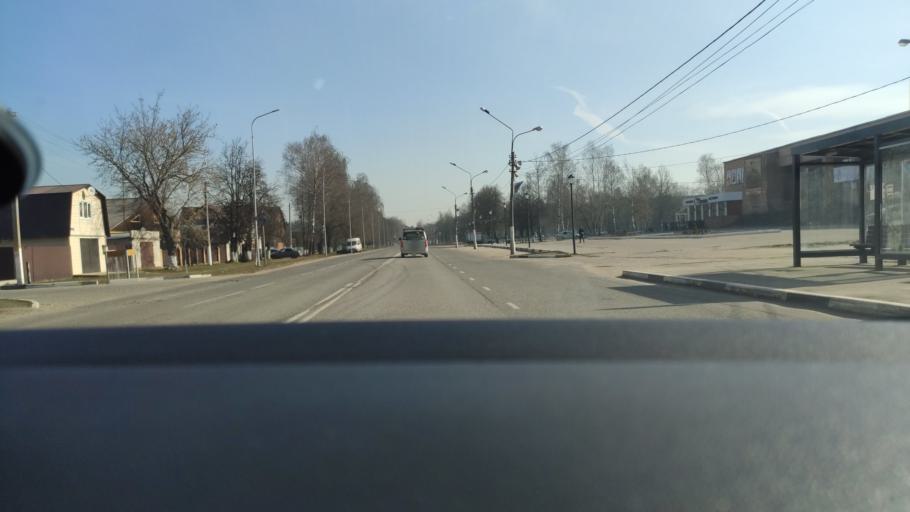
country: RU
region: Moskovskaya
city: Staraya Kupavna
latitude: 55.8118
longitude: 38.1806
